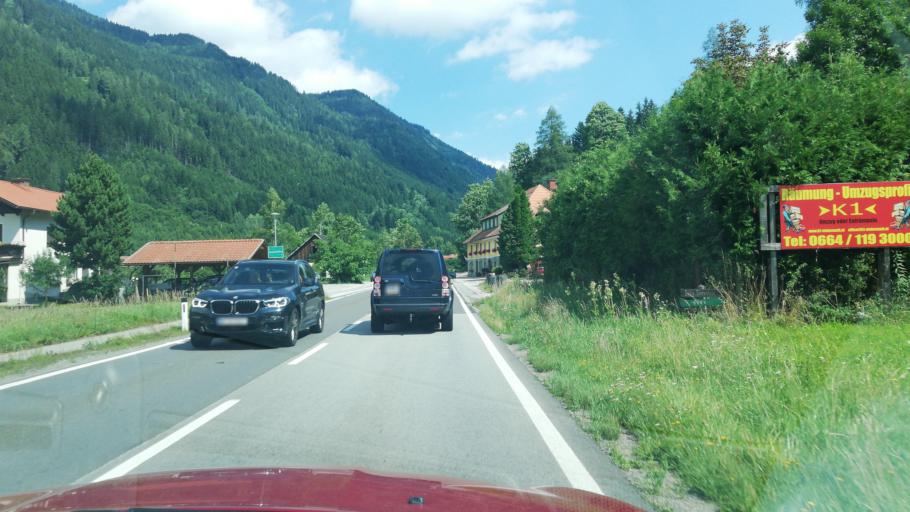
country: AT
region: Styria
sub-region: Politischer Bezirk Murau
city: Durnstein in der Steiermark
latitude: 46.9942
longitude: 14.3907
